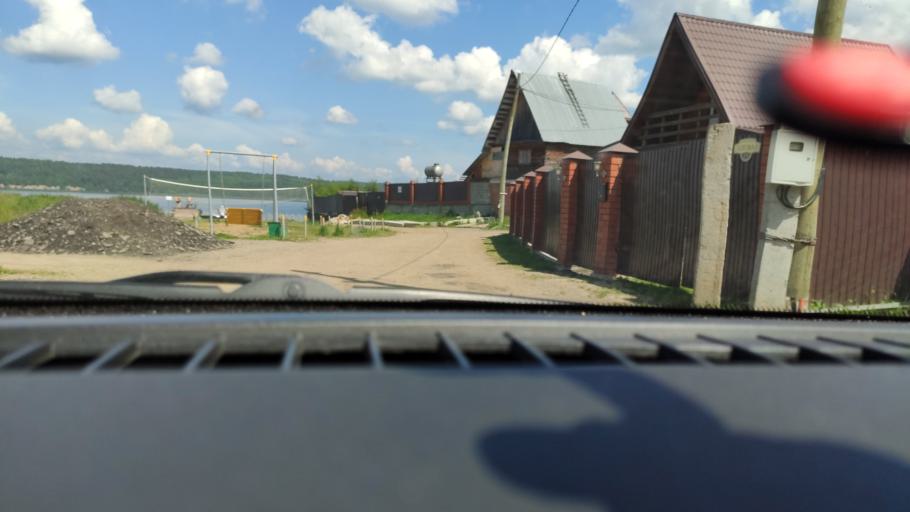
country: RU
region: Perm
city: Sylva
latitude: 58.0477
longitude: 56.7264
